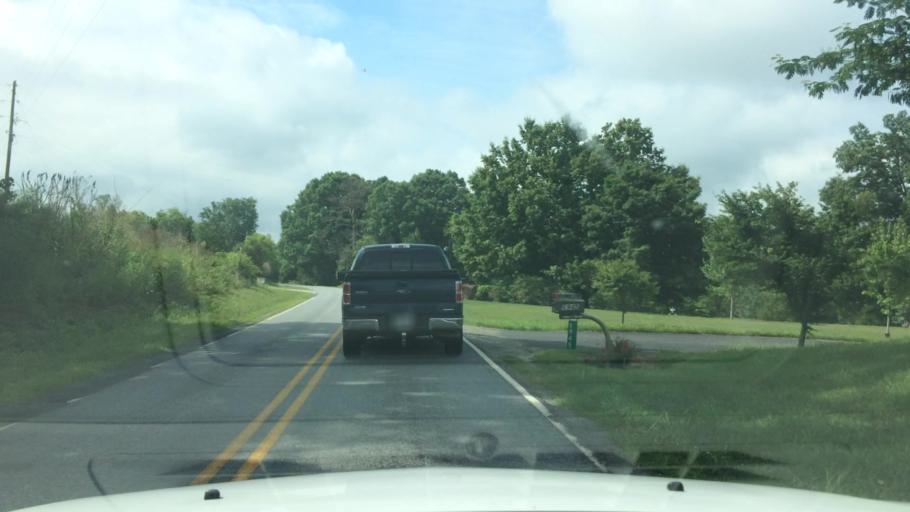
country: US
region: North Carolina
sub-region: Yadkin County
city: Jonesville
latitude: 36.1160
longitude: -80.8573
